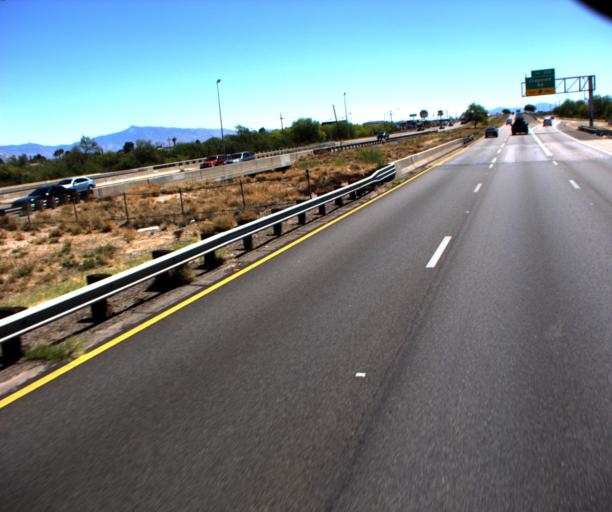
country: US
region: Arizona
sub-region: Pima County
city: Summit
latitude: 32.1290
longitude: -110.8814
